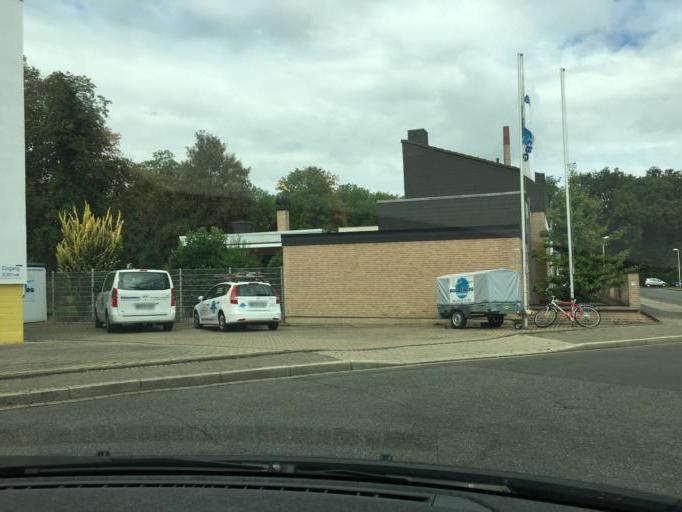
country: DE
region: North Rhine-Westphalia
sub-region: Regierungsbezirk Koln
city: Dueren
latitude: 50.8121
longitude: 6.4697
